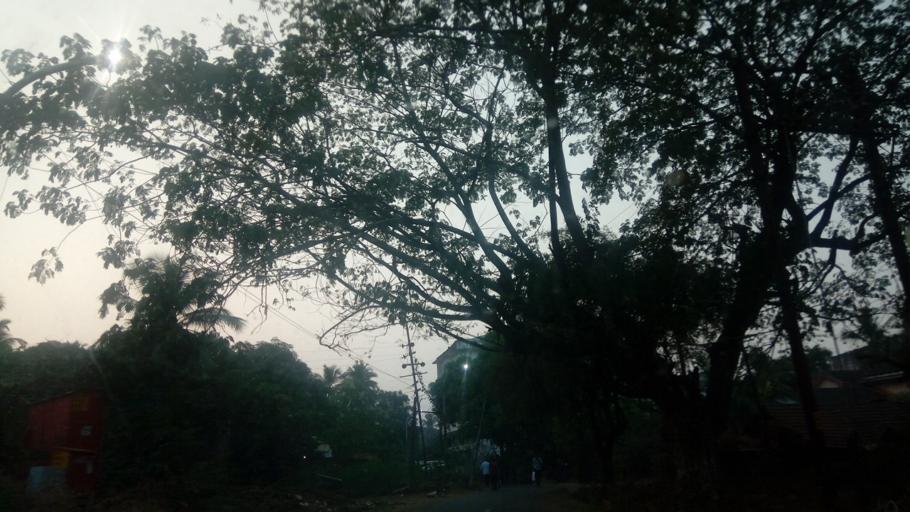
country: IN
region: Goa
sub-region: South Goa
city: Madgaon
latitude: 15.2884
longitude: 73.9615
